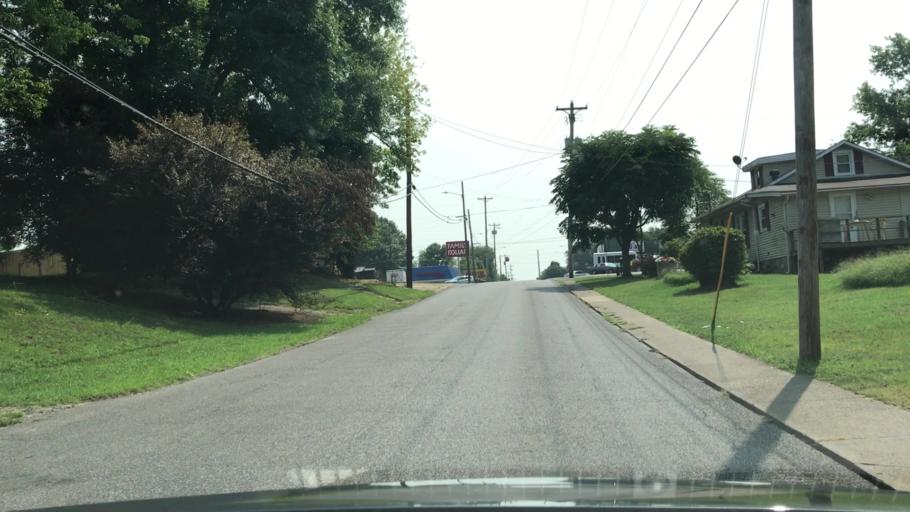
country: US
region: Kentucky
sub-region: Graves County
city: Mayfield
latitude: 36.7297
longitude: -88.6404
